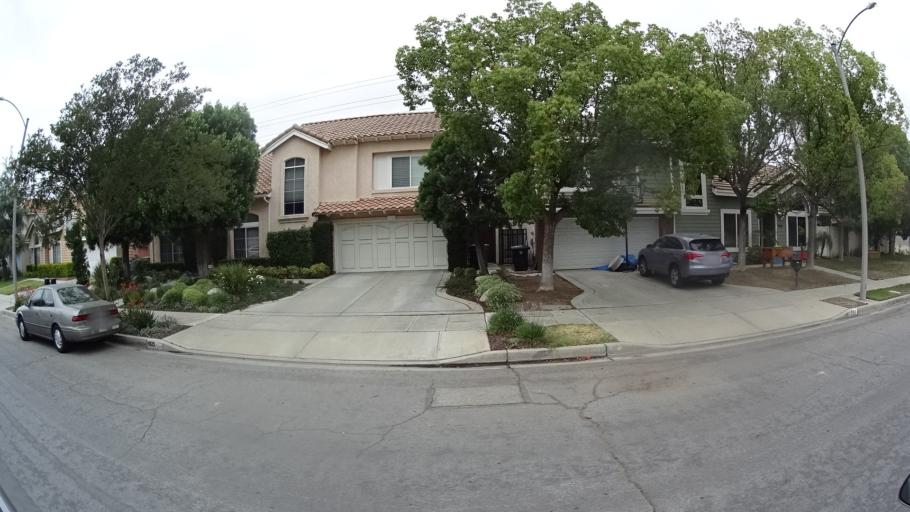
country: US
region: California
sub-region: Los Angeles County
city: Burbank
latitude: 34.1881
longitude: -118.3322
